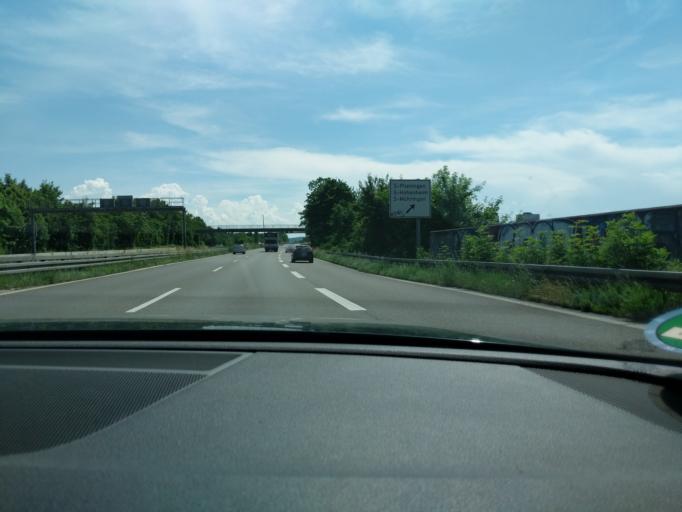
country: DE
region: Baden-Wuerttemberg
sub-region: Regierungsbezirk Stuttgart
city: Leinfelden-Echterdingen
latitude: 48.7286
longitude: 9.1664
